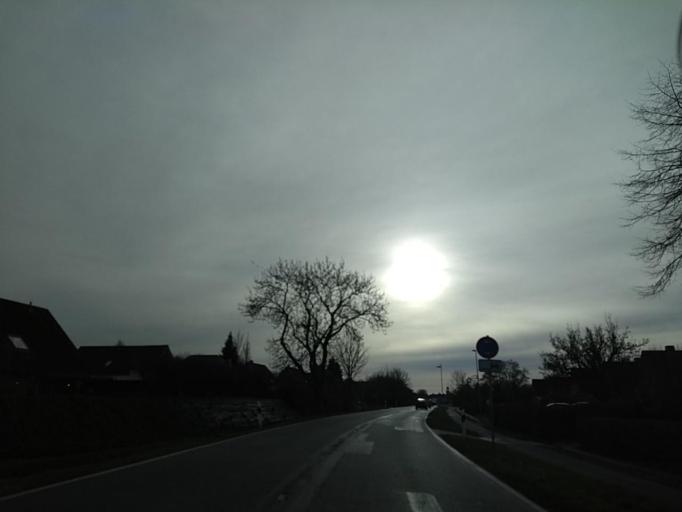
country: DE
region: Lower Saxony
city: Jemgum
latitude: 53.2739
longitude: 7.3860
